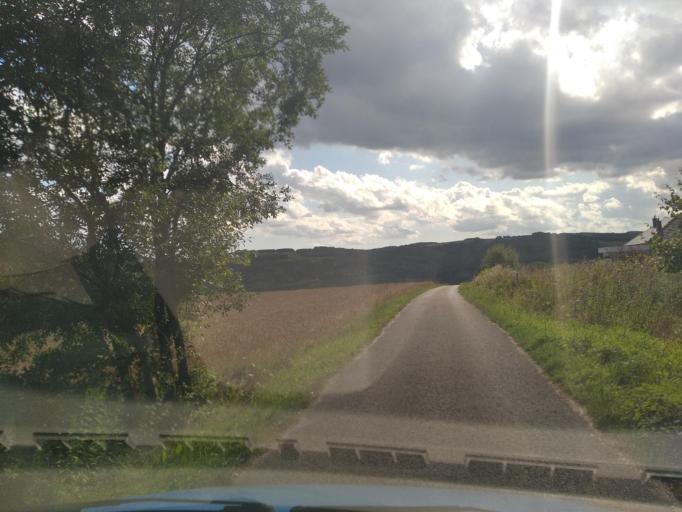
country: PL
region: Subcarpathian Voivodeship
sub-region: Powiat strzyzowski
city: Polomia
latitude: 49.8927
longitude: 21.9066
